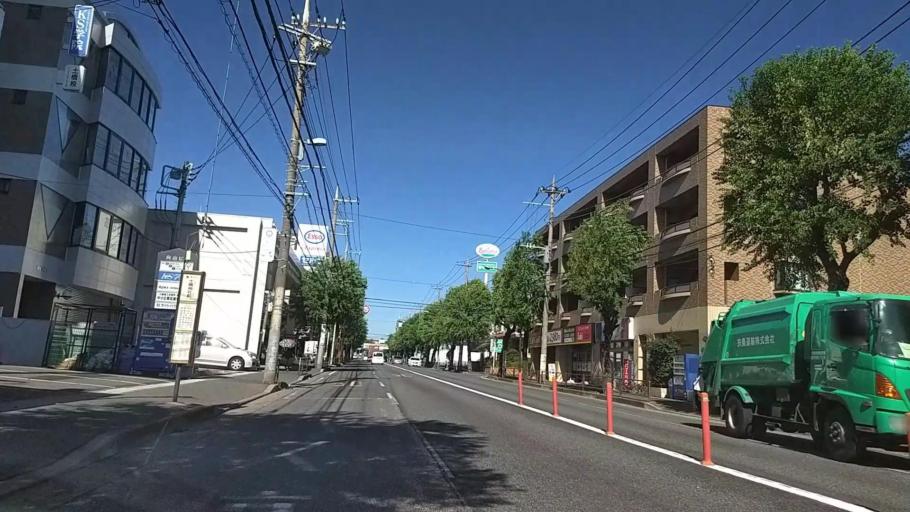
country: JP
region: Tokyo
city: Chofugaoka
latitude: 35.5861
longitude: 139.5764
